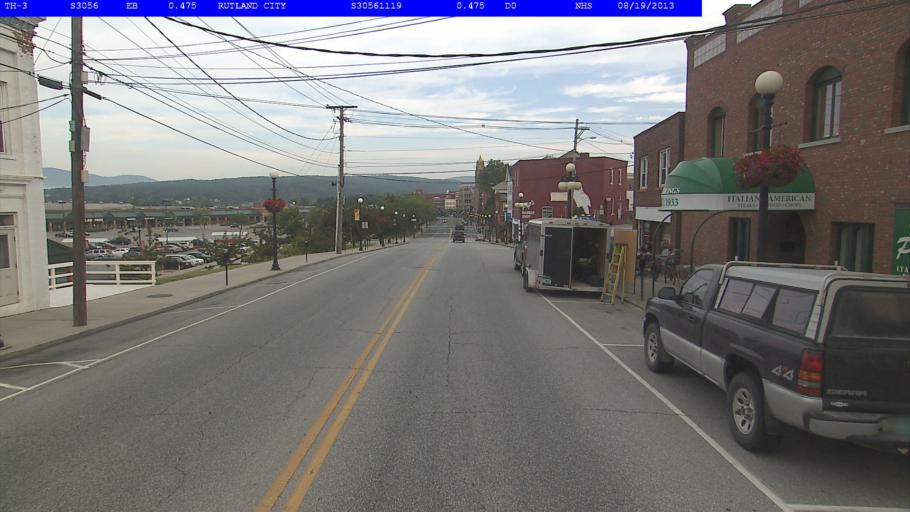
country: US
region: Vermont
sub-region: Rutland County
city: Rutland
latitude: 43.6040
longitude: -72.9769
